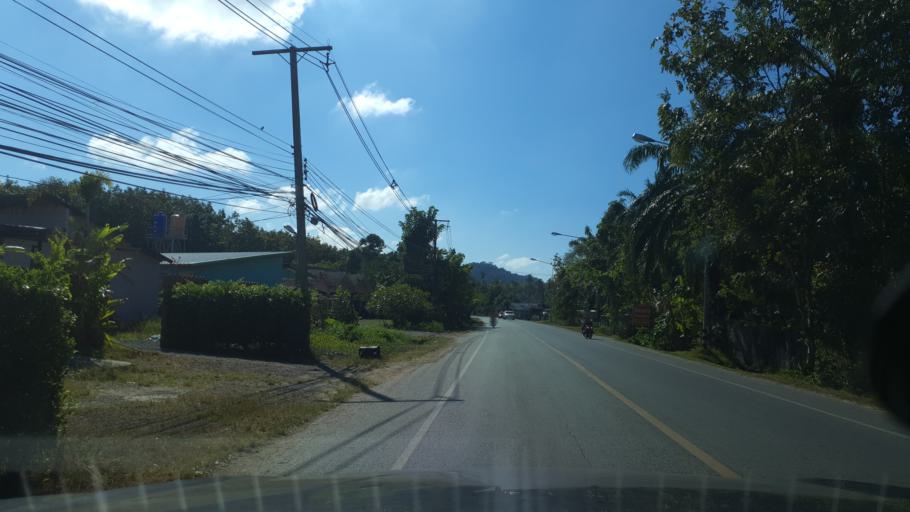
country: TH
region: Phangnga
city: Ban Ao Nang
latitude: 8.0566
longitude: 98.8147
